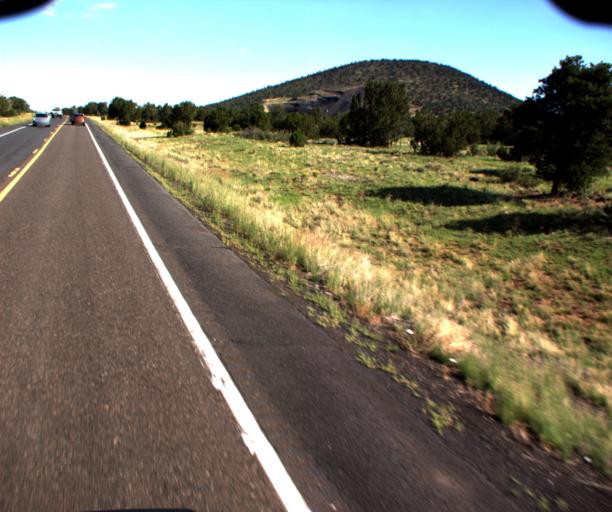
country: US
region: Arizona
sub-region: Coconino County
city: Williams
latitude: 35.3327
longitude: -112.1581
